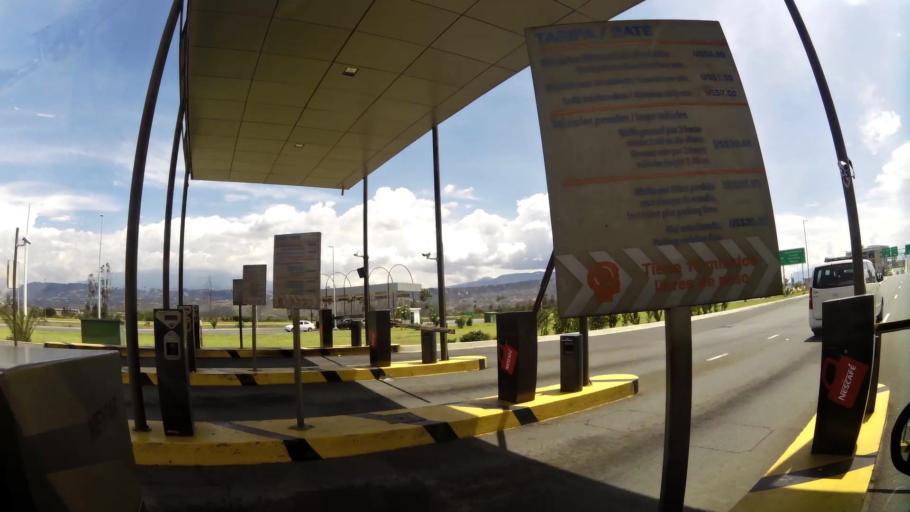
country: EC
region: Pichincha
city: Quito
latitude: -0.1287
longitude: -78.3608
